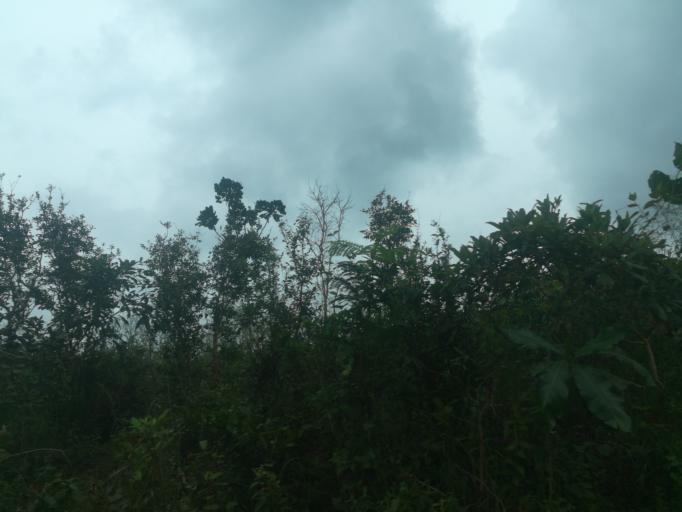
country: NG
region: Ogun
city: Ayetoro
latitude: 7.1045
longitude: 3.1447
